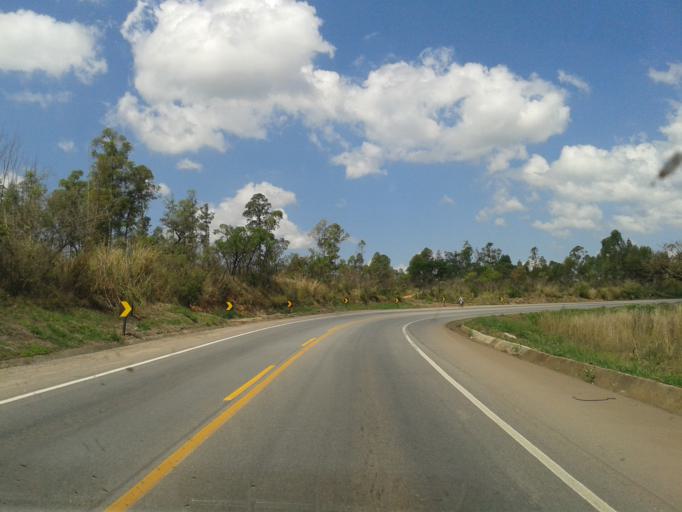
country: BR
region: Minas Gerais
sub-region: Campos Altos
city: Campos Altos
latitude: -19.6719
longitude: -46.0446
